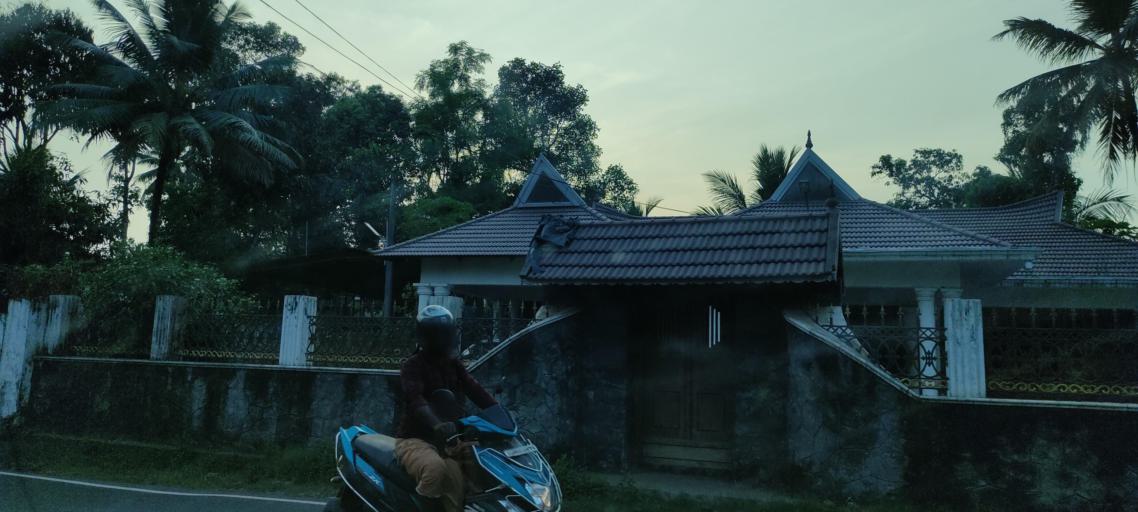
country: IN
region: Kerala
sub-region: Alappuzha
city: Mavelikara
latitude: 9.2685
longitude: 76.5408
